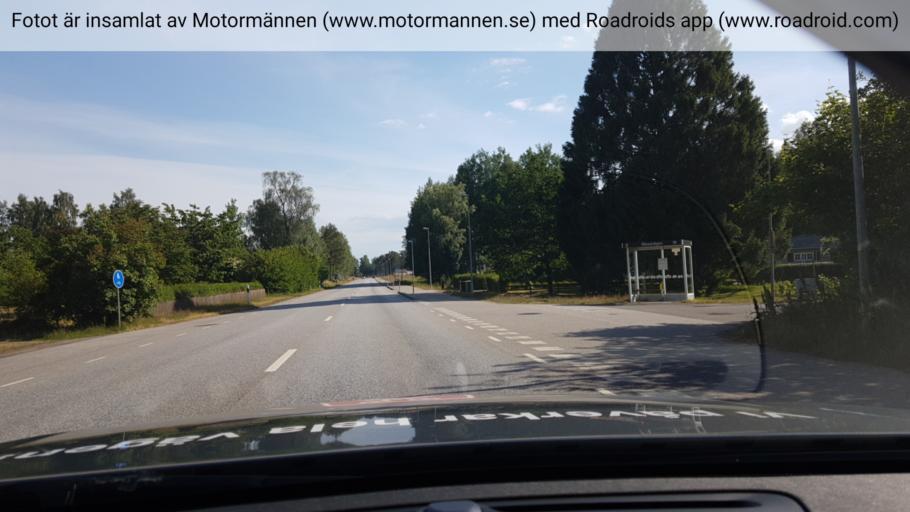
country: SE
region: Vaestra Goetaland
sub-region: Karlsborgs Kommun
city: Karlsborg
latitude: 58.5552
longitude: 14.5008
